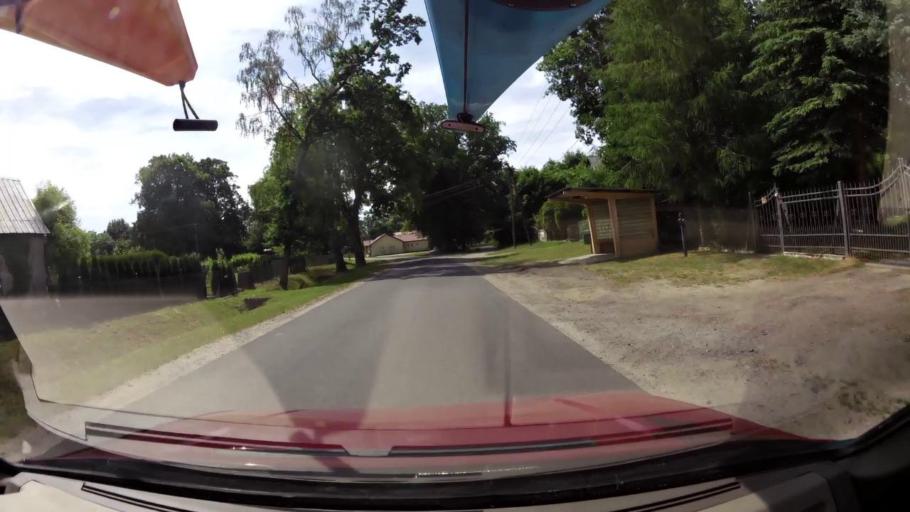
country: PL
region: West Pomeranian Voivodeship
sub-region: Powiat slawienski
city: Darlowo
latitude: 54.3070
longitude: 16.4796
